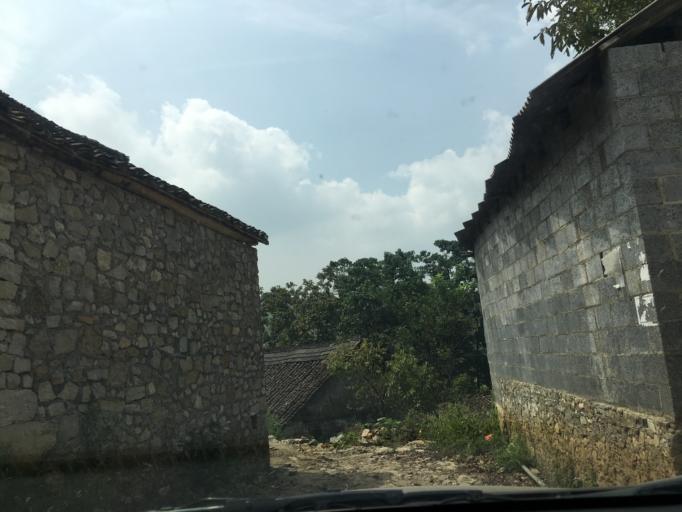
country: CN
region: Guizhou Sheng
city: Anshun
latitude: 25.5964
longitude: 105.6748
